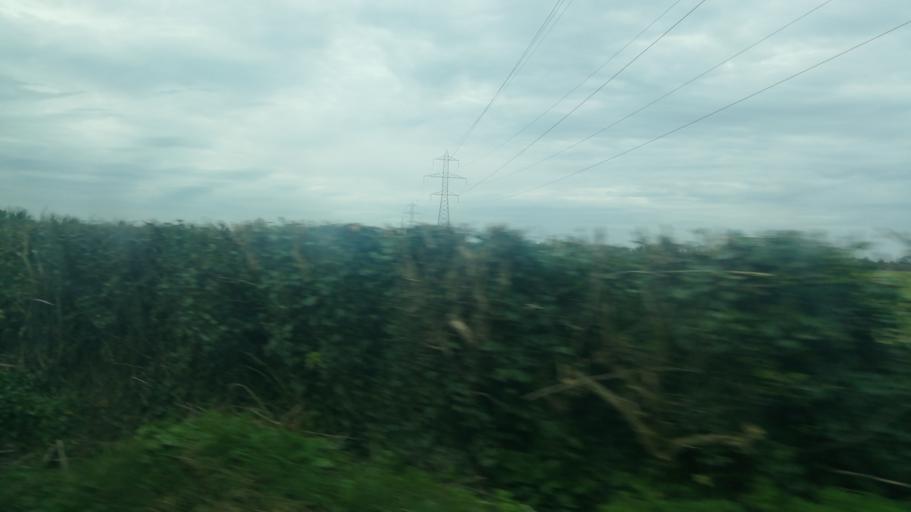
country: IE
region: Leinster
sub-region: Kildare
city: Maynooth
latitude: 53.3504
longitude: -6.6037
